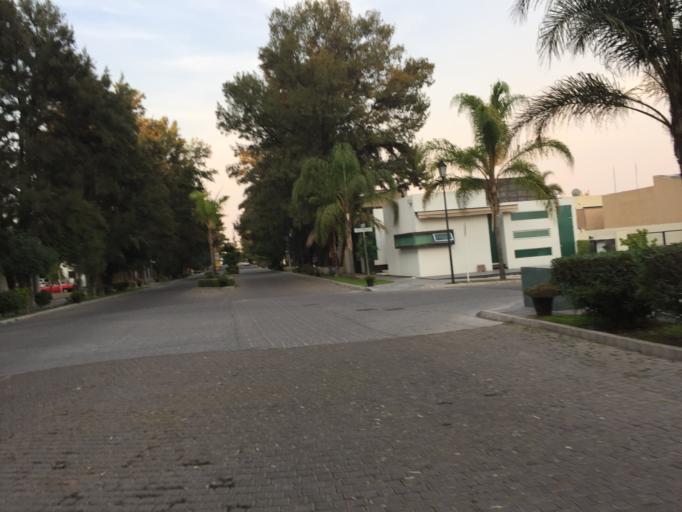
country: MX
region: Aguascalientes
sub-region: Aguascalientes
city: La Loma de los Negritos
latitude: 21.8505
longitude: -102.3570
